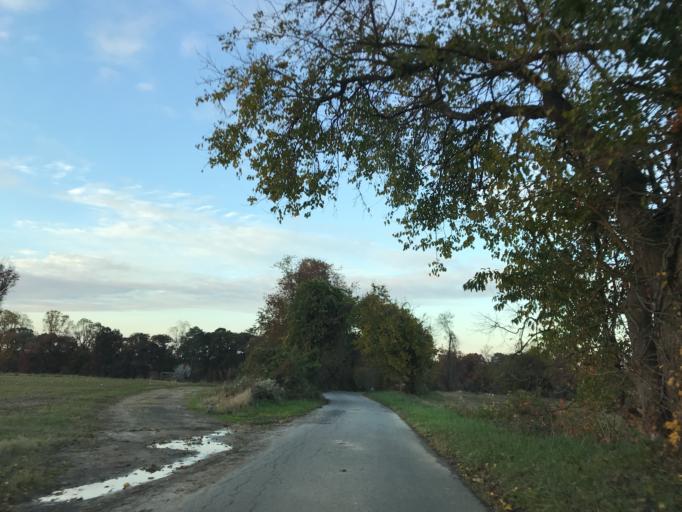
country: US
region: Maryland
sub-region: Baltimore County
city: White Marsh
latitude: 39.3761
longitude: -76.4012
